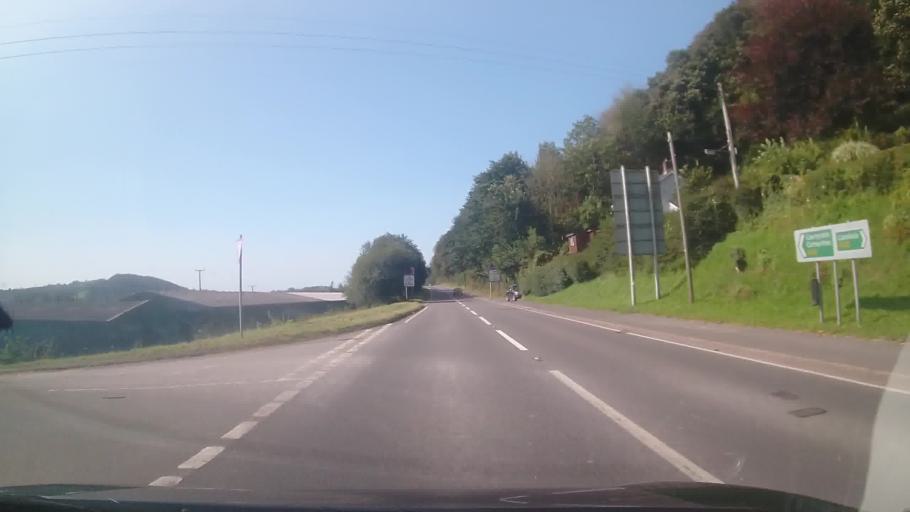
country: GB
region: Wales
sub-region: Carmarthenshire
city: Carmarthen
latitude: 51.8683
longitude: -4.2406
